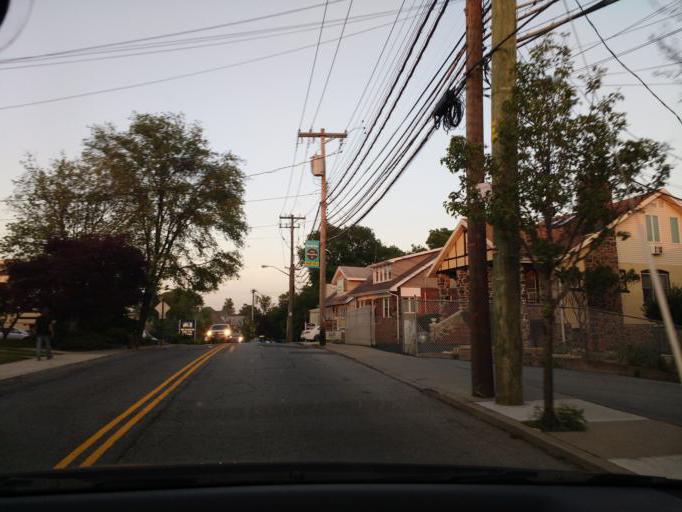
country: US
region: New York
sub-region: Richmond County
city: Staten Island
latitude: 40.5516
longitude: -74.1488
